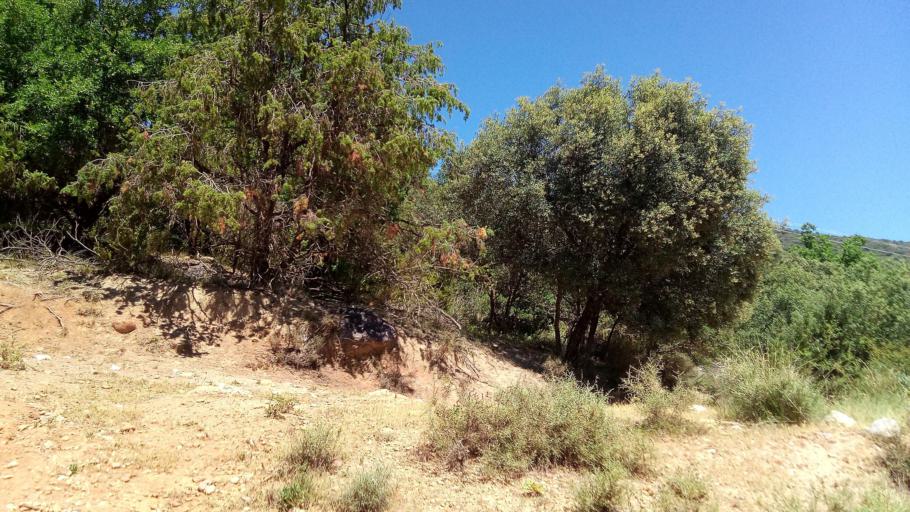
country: ES
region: Aragon
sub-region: Provincia de Huesca
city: Castigaleu
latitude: 42.3147
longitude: 0.5579
